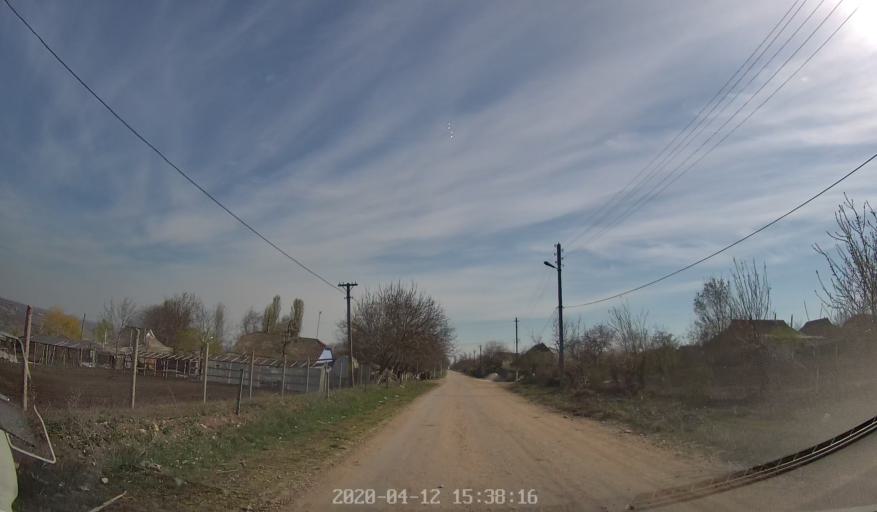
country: MD
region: Telenesti
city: Cocieri
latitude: 47.3193
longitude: 29.0691
